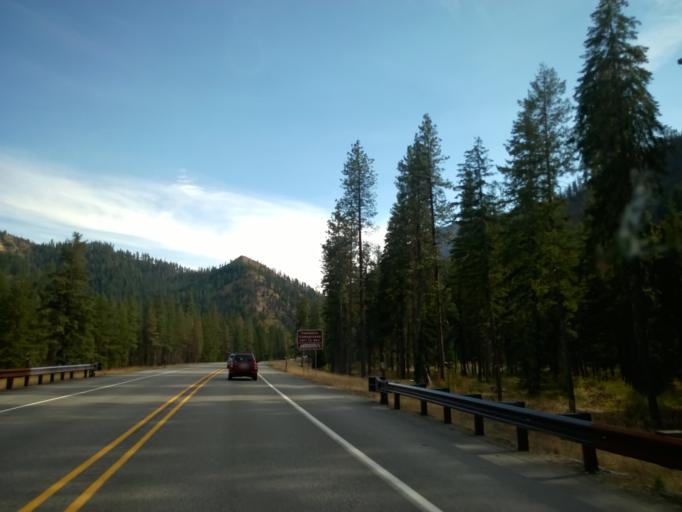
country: US
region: Washington
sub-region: Chelan County
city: Leavenworth
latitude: 47.6853
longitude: -120.7355
